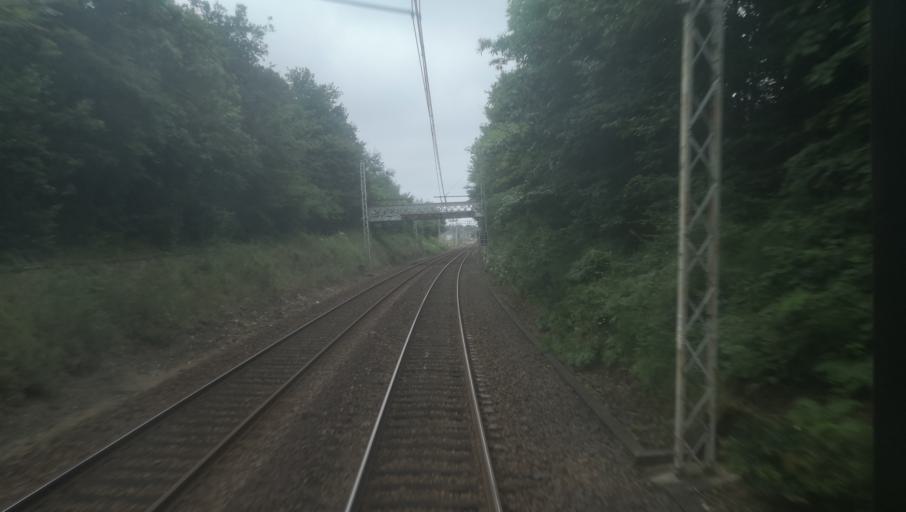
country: FR
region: Centre
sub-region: Departement de l'Indre
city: Chantome
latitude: 46.3812
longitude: 1.5416
